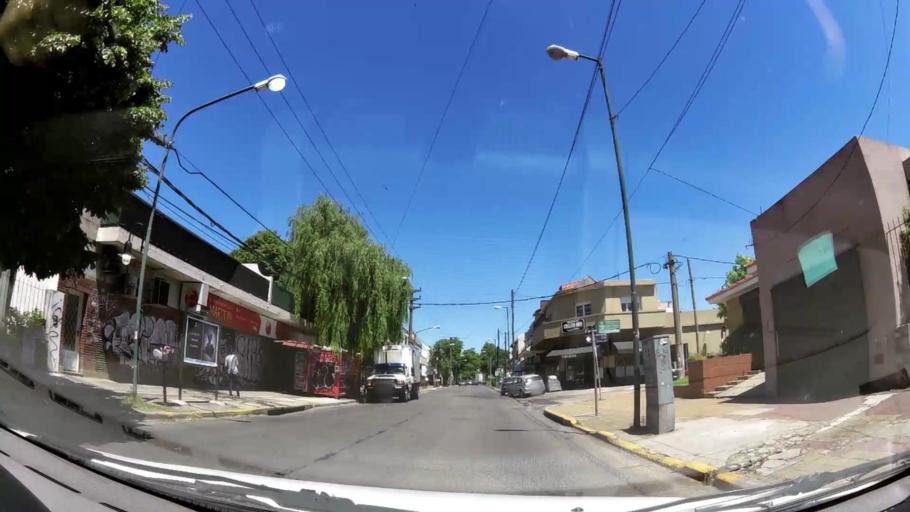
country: AR
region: Buenos Aires
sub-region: Partido de Vicente Lopez
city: Olivos
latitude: -34.5024
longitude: -58.5079
